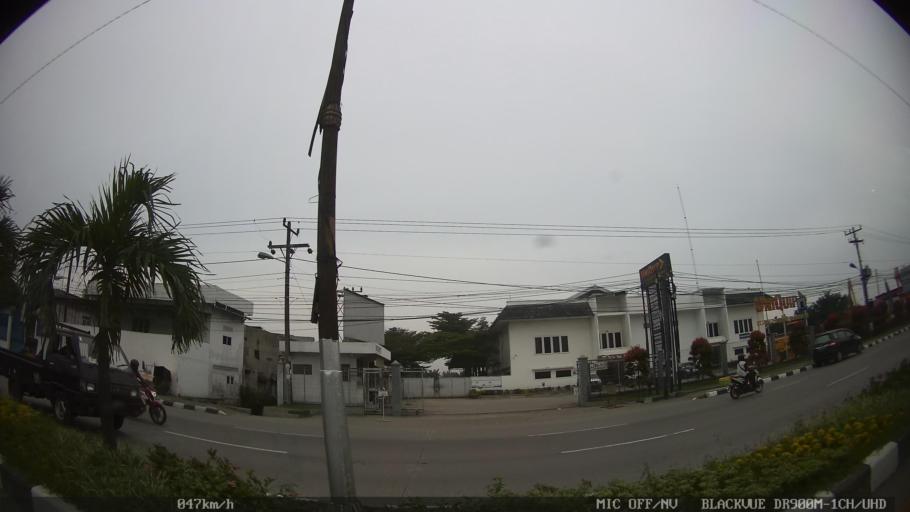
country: ID
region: North Sumatra
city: Deli Tua
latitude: 3.5391
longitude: 98.7040
